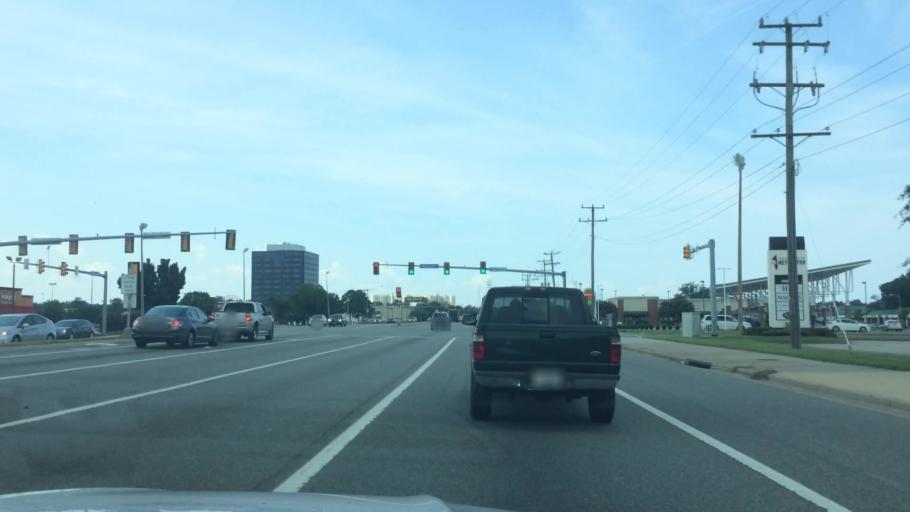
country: US
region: Virginia
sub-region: City of Newport News
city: Newport News
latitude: 37.0223
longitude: -76.4389
